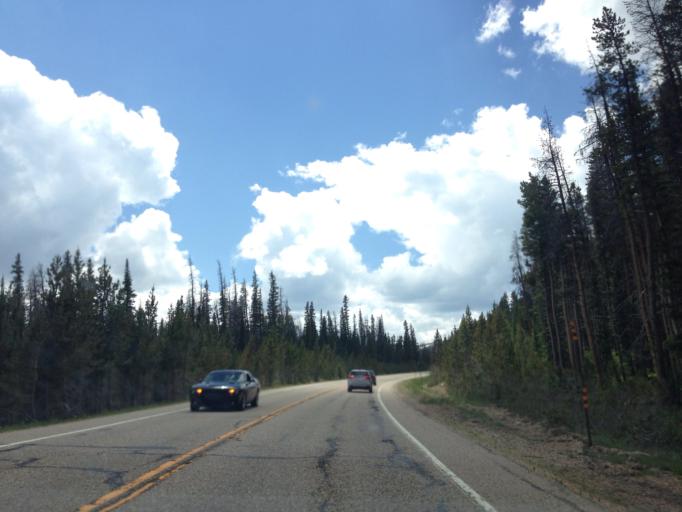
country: US
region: Colorado
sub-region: Larimer County
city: Estes Park
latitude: 40.5647
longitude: -105.8646
